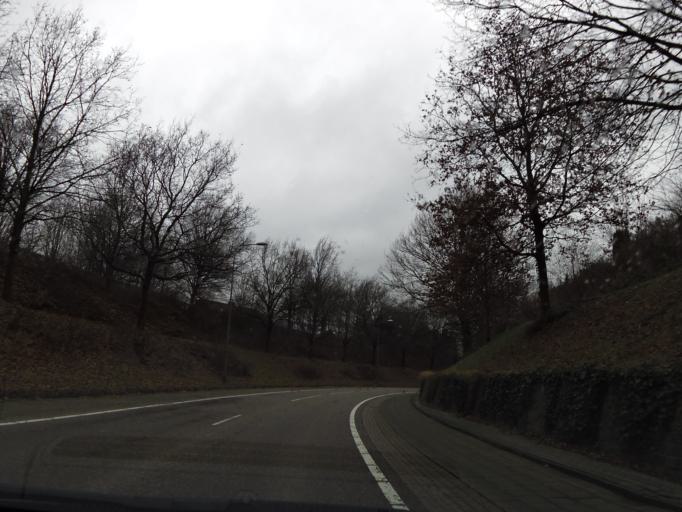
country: NL
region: Limburg
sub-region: Gemeente Vaals
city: Vaals
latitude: 50.7755
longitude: 6.0055
